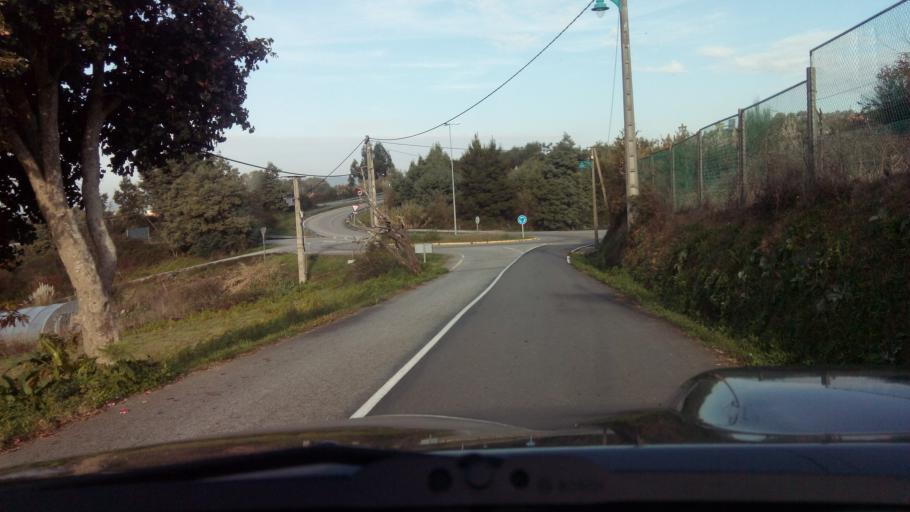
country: ES
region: Galicia
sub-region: Provincia de Pontevedra
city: Marin
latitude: 42.3661
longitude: -8.7195
